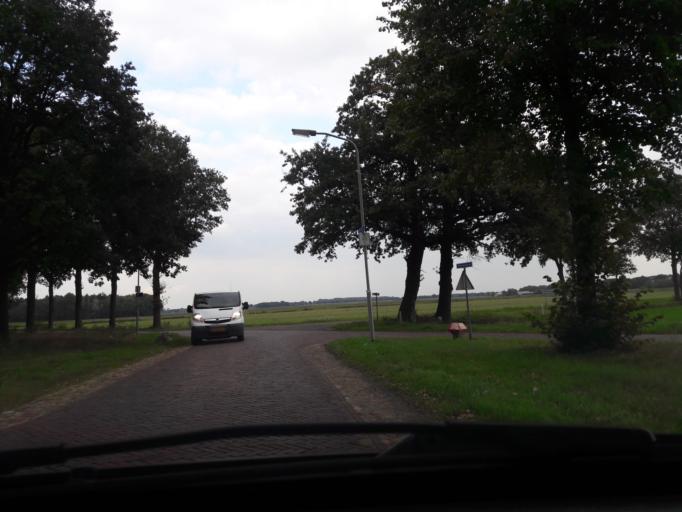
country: NL
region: Drenthe
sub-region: Gemeente Borger-Odoorn
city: Borger
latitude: 52.9514
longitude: 6.8241
